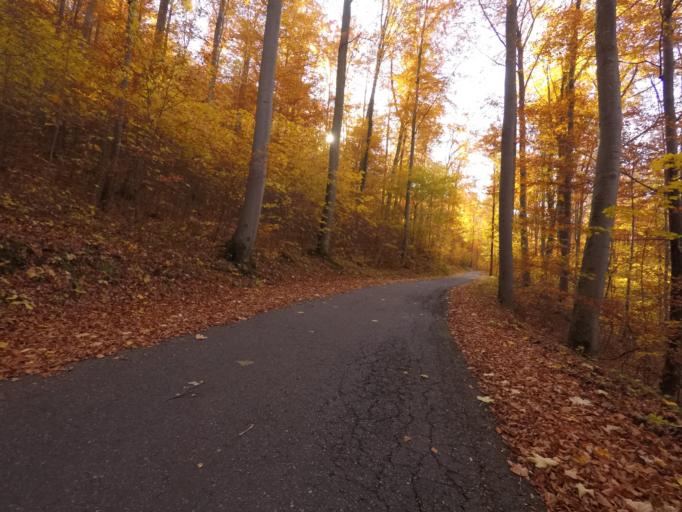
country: DE
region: Baden-Wuerttemberg
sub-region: Tuebingen Region
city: Pfullingen
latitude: 48.4401
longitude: 9.2376
